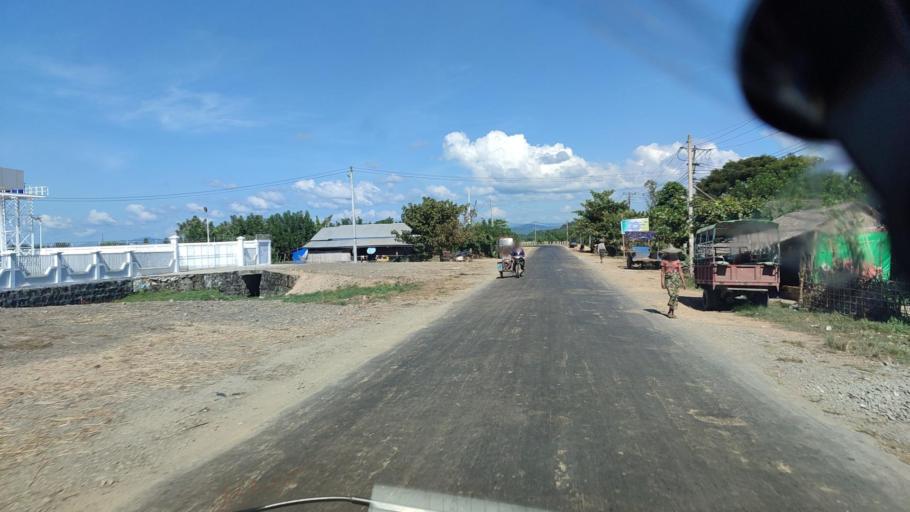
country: MM
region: Rakhine
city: Sittwe
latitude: 20.4089
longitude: 93.3037
